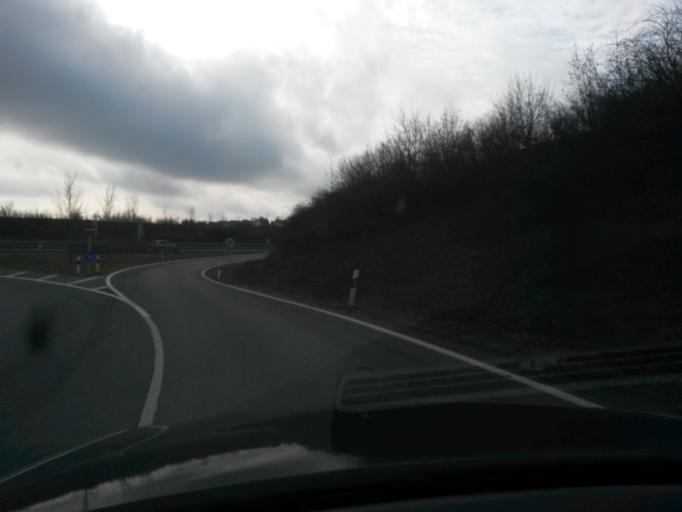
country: DE
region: Bavaria
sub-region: Regierungsbezirk Unterfranken
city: Estenfeld
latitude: 49.8399
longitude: 9.9999
